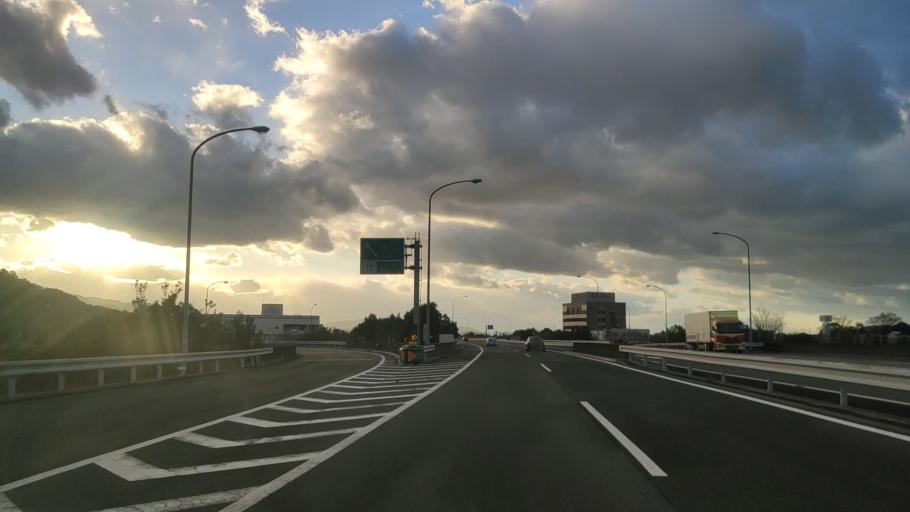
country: JP
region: Ehime
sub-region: Shikoku-chuo Shi
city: Matsuyama
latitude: 33.7946
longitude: 132.9057
